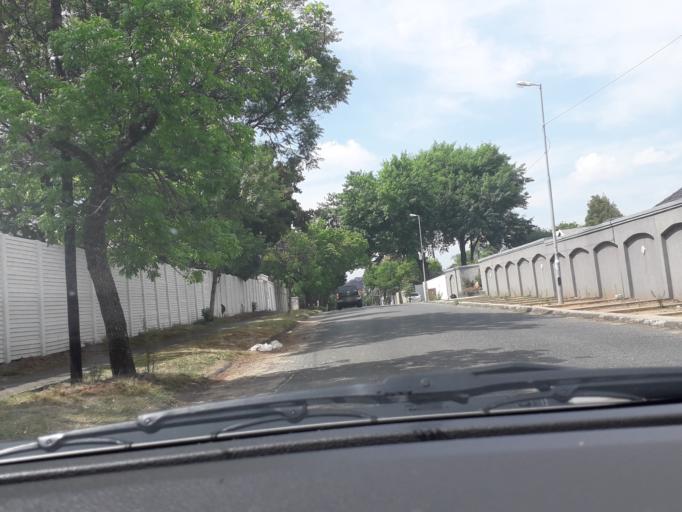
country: ZA
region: Gauteng
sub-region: City of Johannesburg Metropolitan Municipality
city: Johannesburg
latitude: -26.1249
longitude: 28.0768
